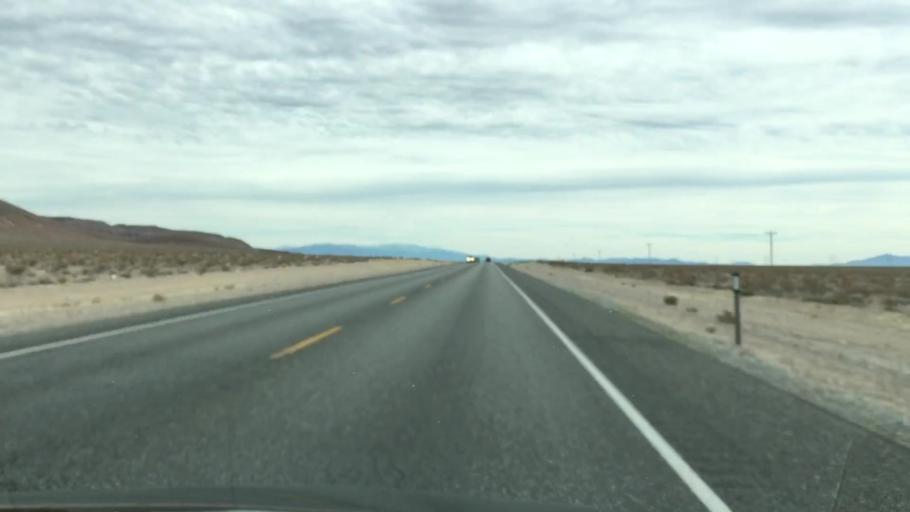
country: US
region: Nevada
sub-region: Nye County
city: Beatty
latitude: 36.7028
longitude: -116.5861
